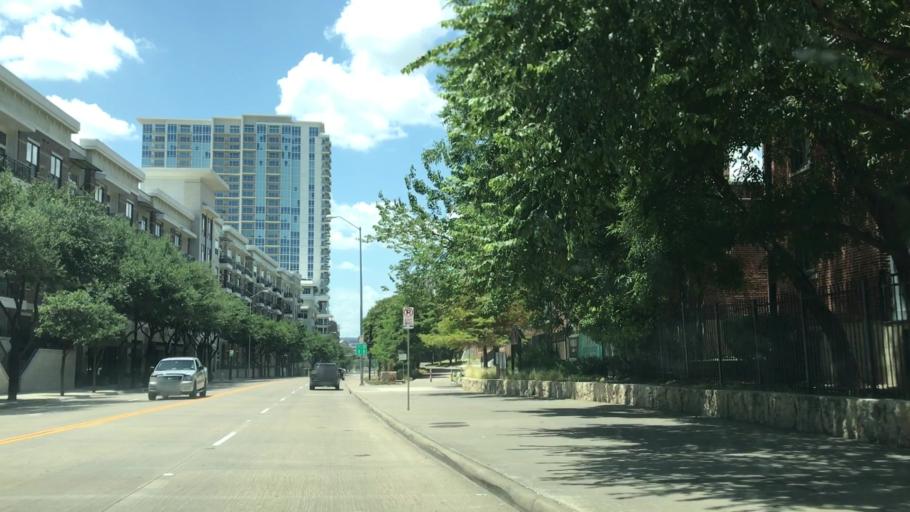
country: US
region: Texas
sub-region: Dallas County
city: Dallas
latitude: 32.7920
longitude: -96.8107
